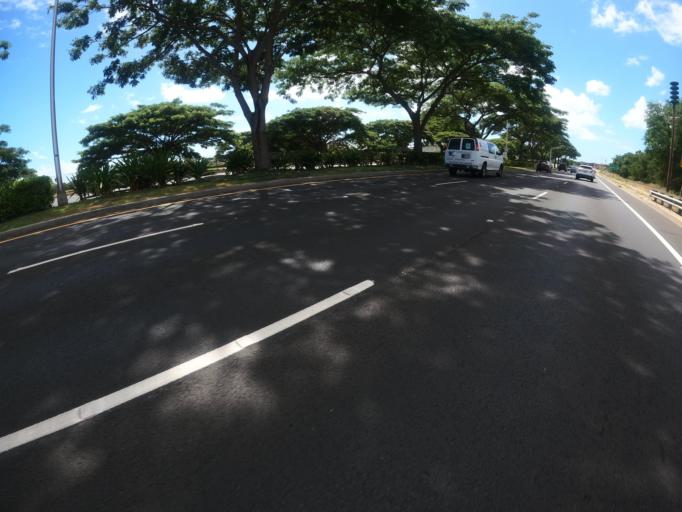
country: US
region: Hawaii
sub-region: Honolulu County
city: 'Ewa Gentry
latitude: 21.3634
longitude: -158.0276
